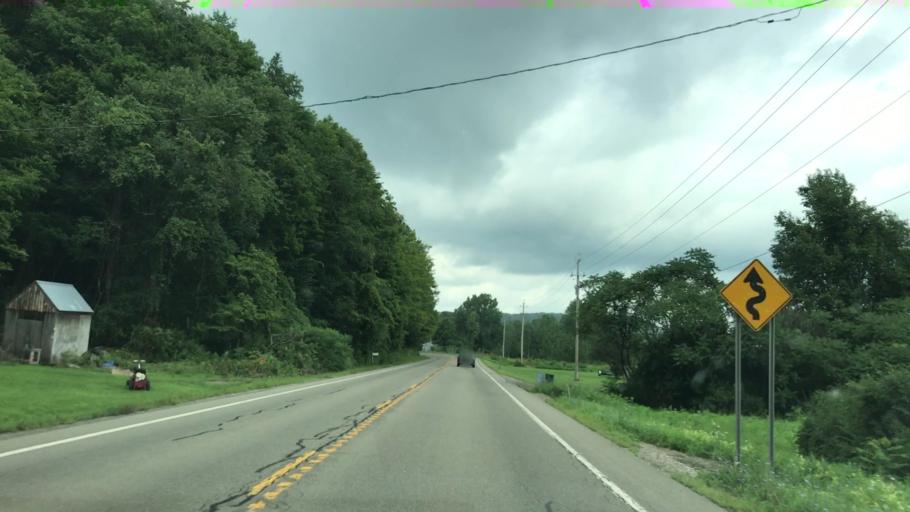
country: US
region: New York
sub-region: Steuben County
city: Bath
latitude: 42.3993
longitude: -77.3489
